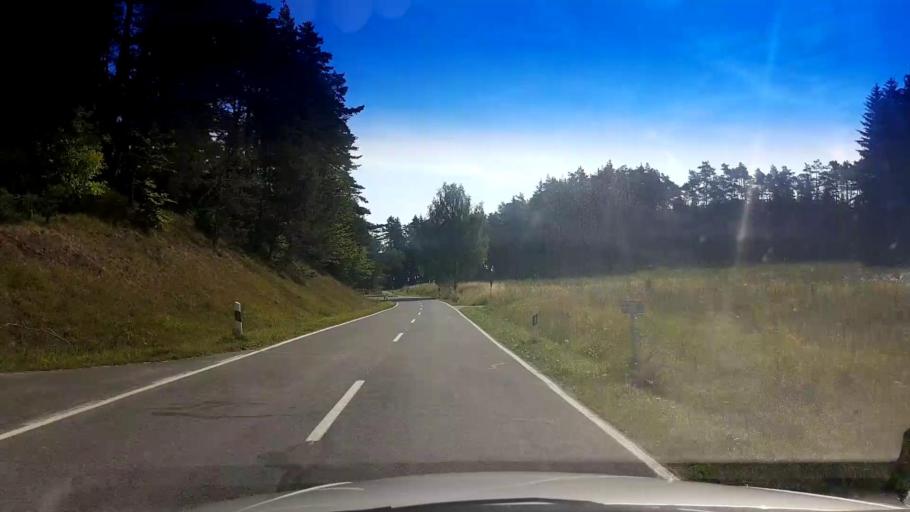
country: DE
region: Bavaria
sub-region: Upper Franconia
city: Stadelhofen
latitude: 49.9693
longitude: 11.2038
